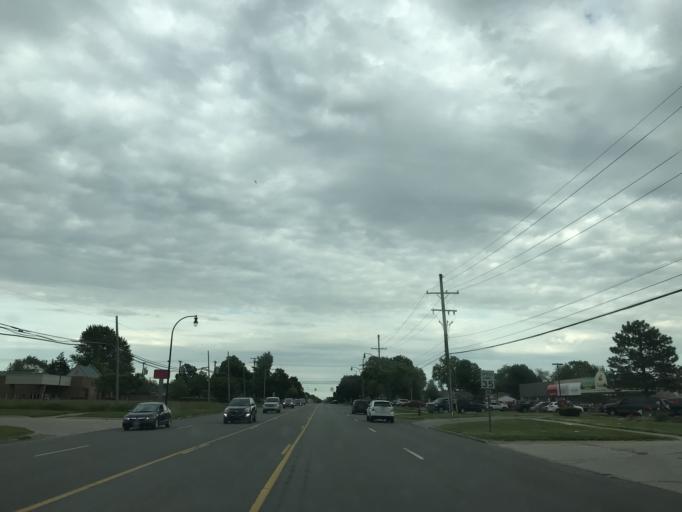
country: US
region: Michigan
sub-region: Wayne County
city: Woodhaven
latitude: 42.1409
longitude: -83.2186
